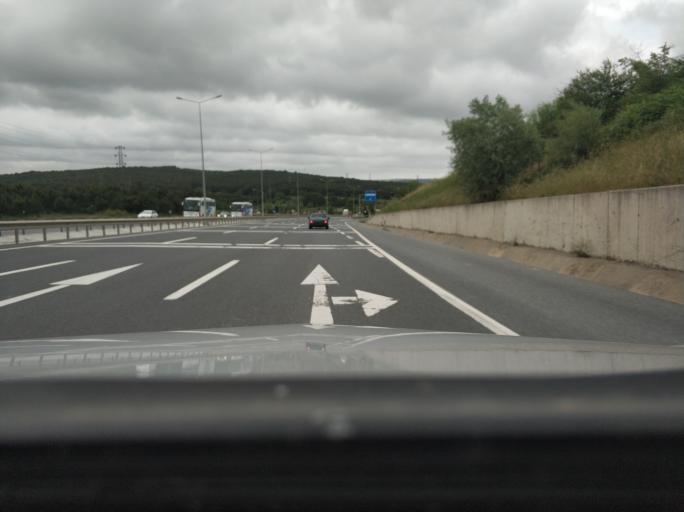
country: TR
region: Istanbul
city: Kemerburgaz
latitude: 41.1592
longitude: 28.8946
